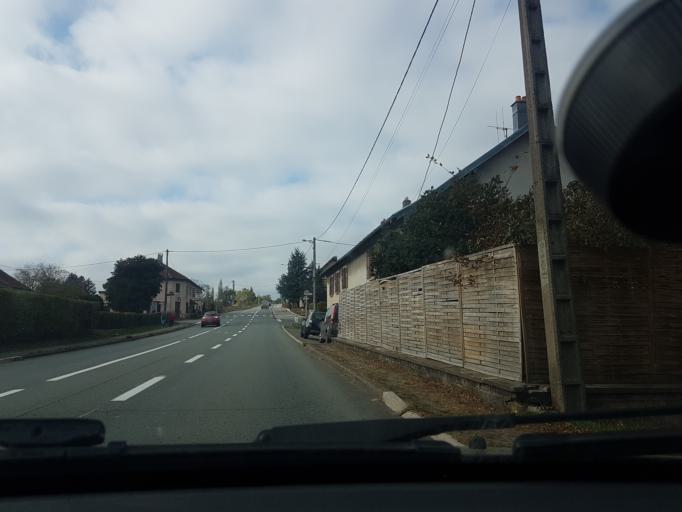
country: FR
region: Franche-Comte
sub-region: Departement de la Haute-Saone
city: Chalonvillars
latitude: 47.6420
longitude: 6.7940
